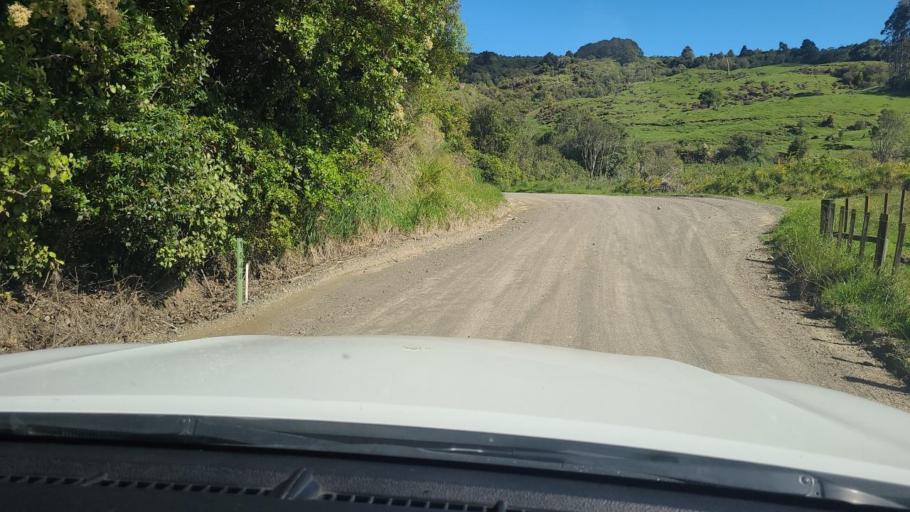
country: NZ
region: Hawke's Bay
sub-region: Napier City
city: Napier
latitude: -39.1069
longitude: 176.8036
